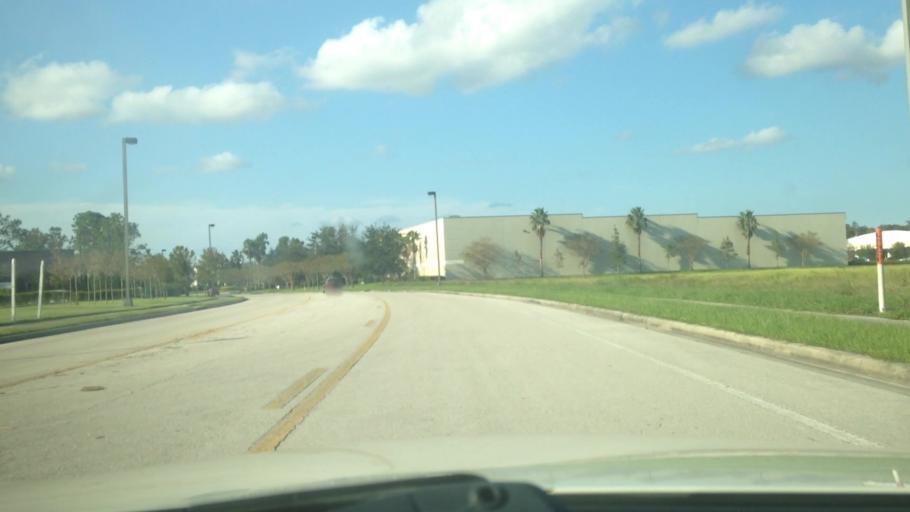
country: US
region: Florida
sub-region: Orange County
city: Conway
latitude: 28.4572
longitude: -81.2958
